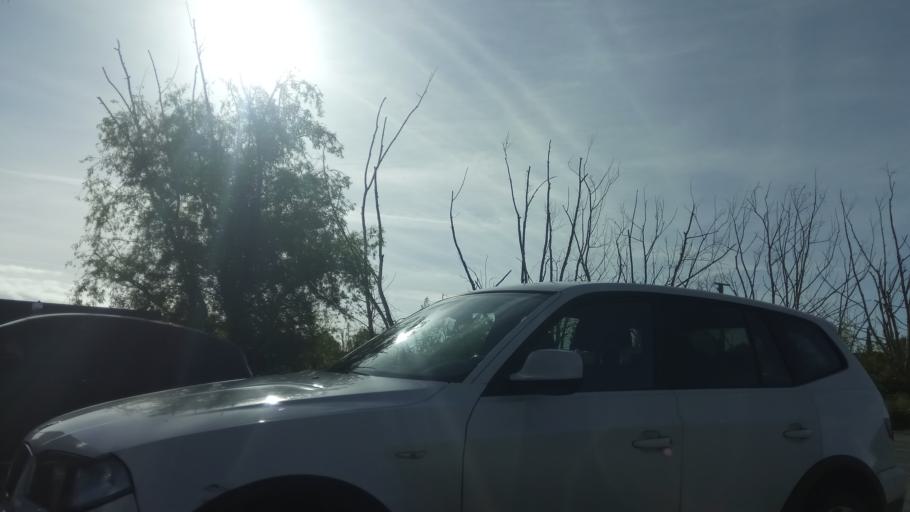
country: IT
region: Latium
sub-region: Provincia di Latina
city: Grunuovo-Campomaggiore San Luca
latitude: 41.2726
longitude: 13.7893
